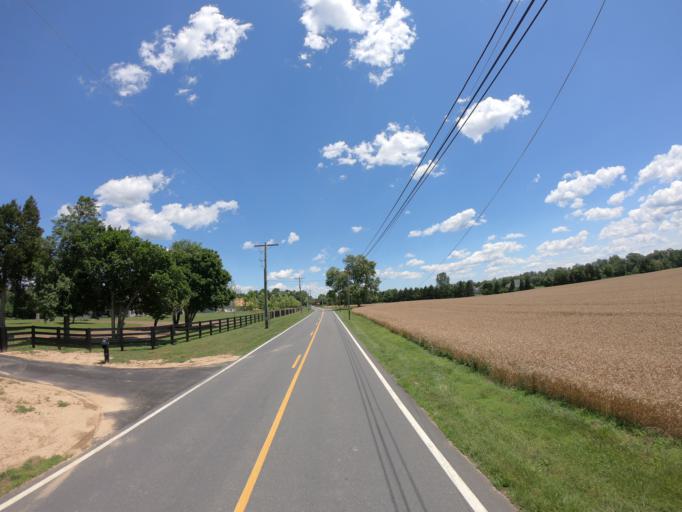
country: US
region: Delaware
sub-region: New Castle County
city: Middletown
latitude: 39.4612
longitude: -75.7533
